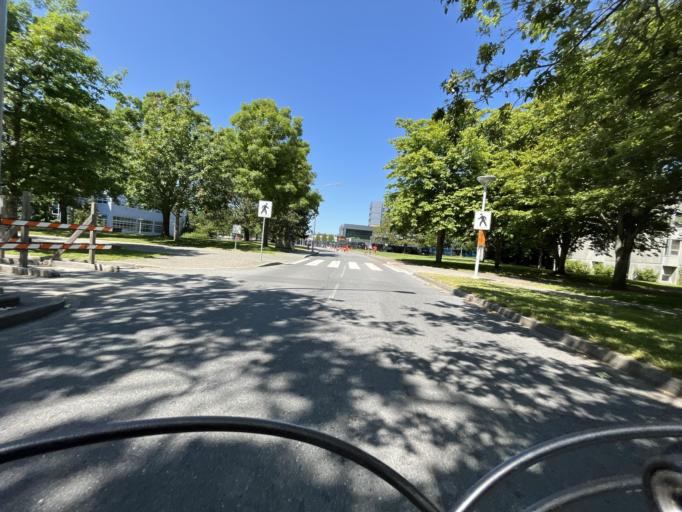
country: CA
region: British Columbia
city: Oak Bay
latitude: 48.4630
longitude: -123.3080
